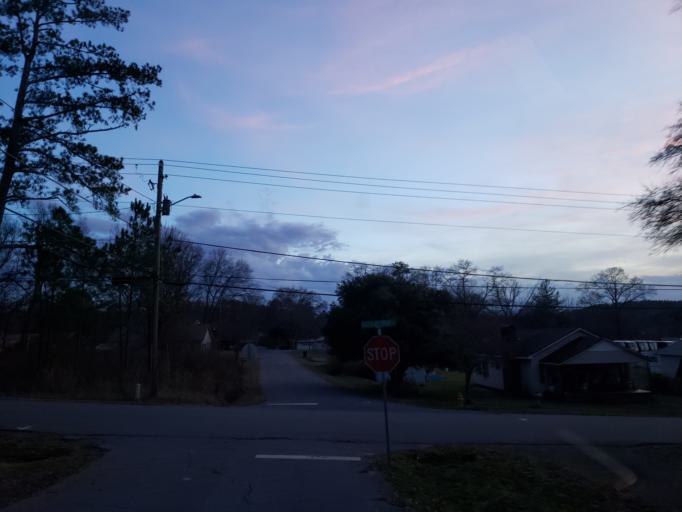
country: US
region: Georgia
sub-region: Bartow County
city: Emerson
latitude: 34.1273
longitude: -84.7543
